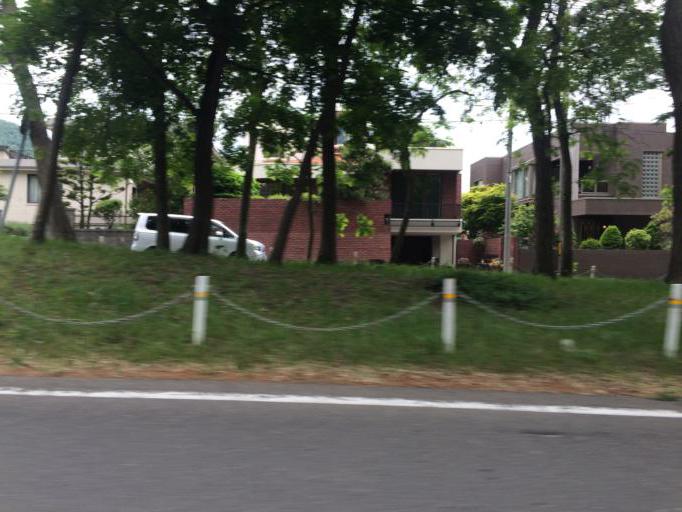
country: JP
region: Hokkaido
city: Sapporo
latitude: 43.0552
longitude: 141.3047
